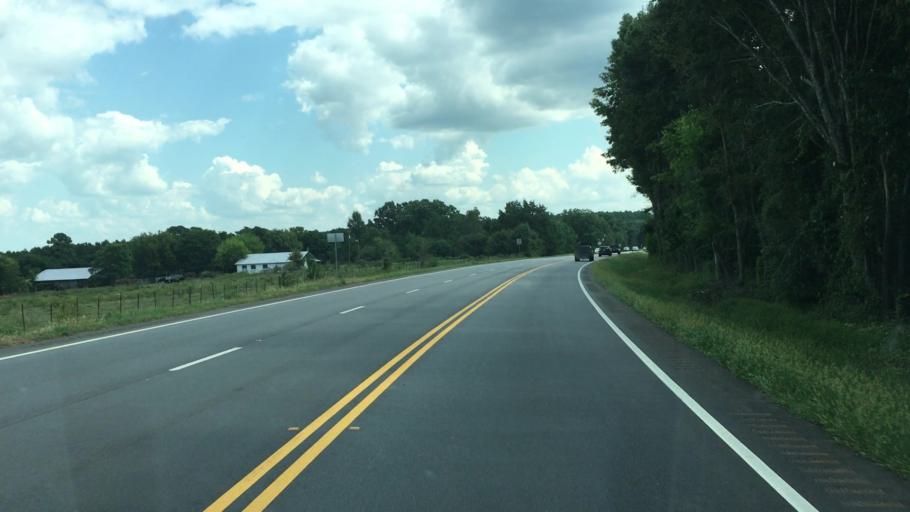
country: US
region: Georgia
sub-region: Putnam County
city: Jefferson
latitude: 33.4684
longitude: -83.4163
